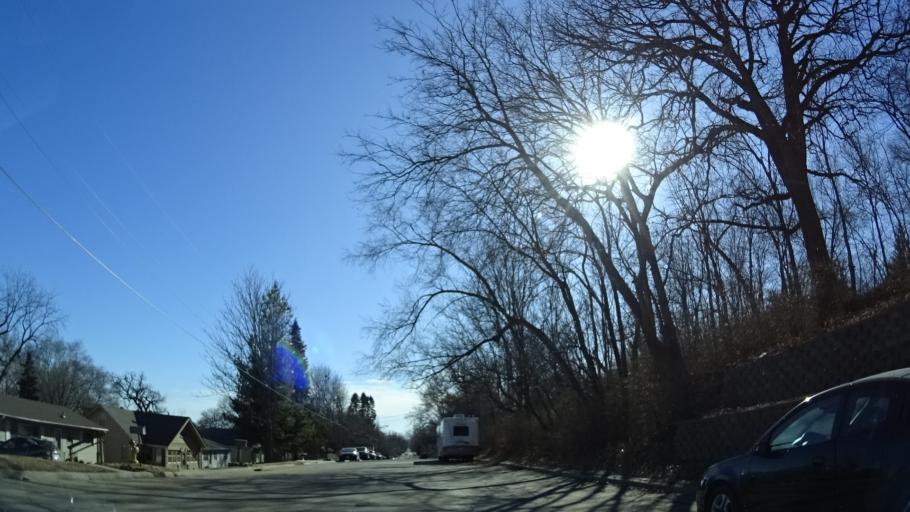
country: US
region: Nebraska
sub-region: Sarpy County
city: Bellevue
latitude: 41.1461
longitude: -95.8937
